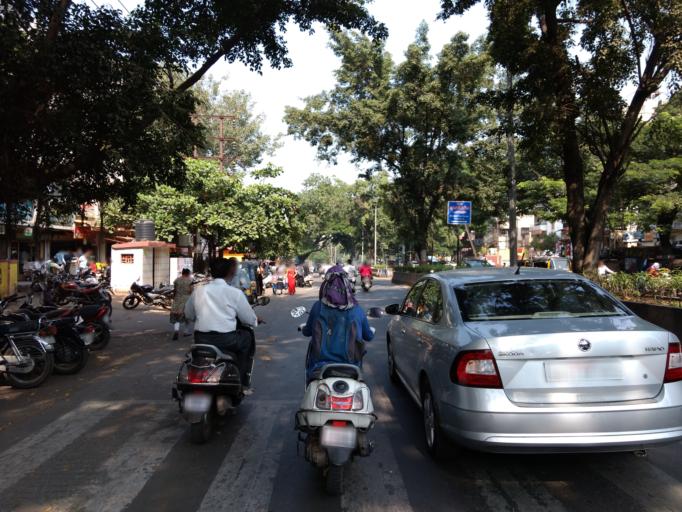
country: IN
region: Maharashtra
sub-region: Pune Division
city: Pune
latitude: 18.4770
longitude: 73.8622
